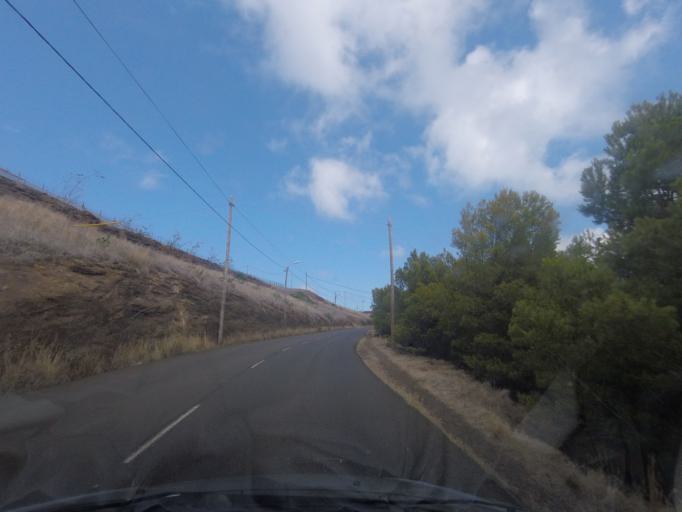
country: PT
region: Madeira
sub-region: Machico
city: Canical
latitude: 32.7438
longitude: -16.7272
